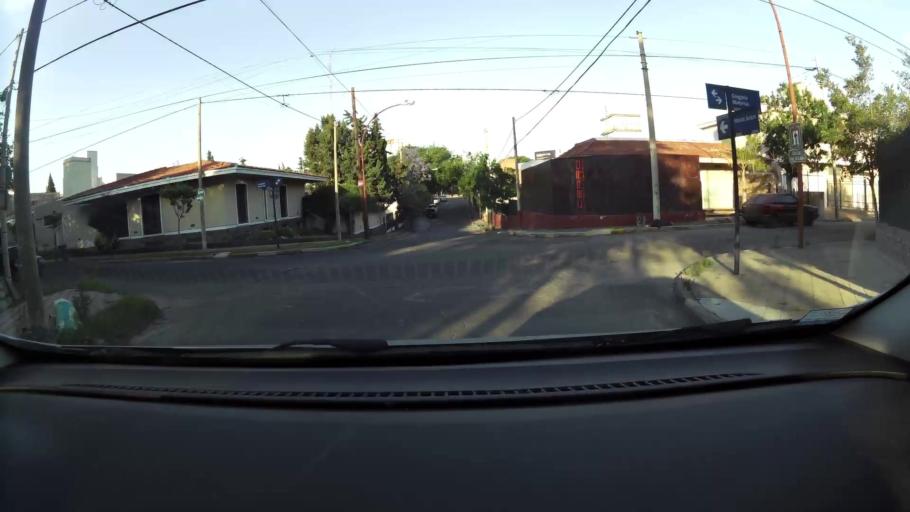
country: AR
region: Cordoba
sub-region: Departamento de Capital
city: Cordoba
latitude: -31.3800
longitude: -64.2247
